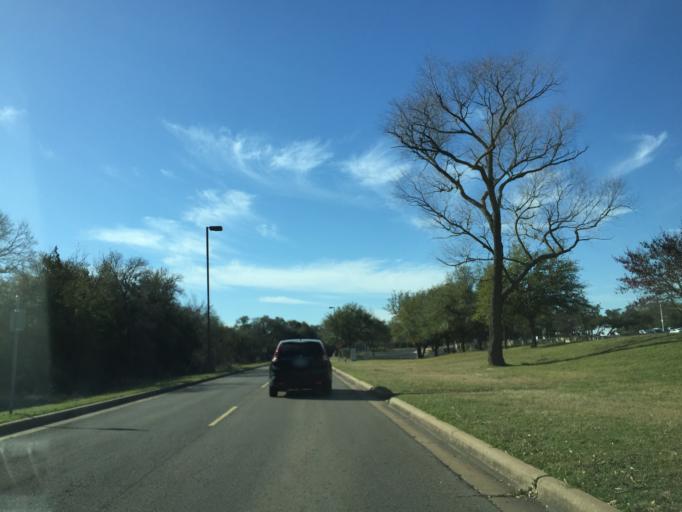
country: US
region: Texas
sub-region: Williamson County
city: Jollyville
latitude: 30.4326
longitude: -97.7500
